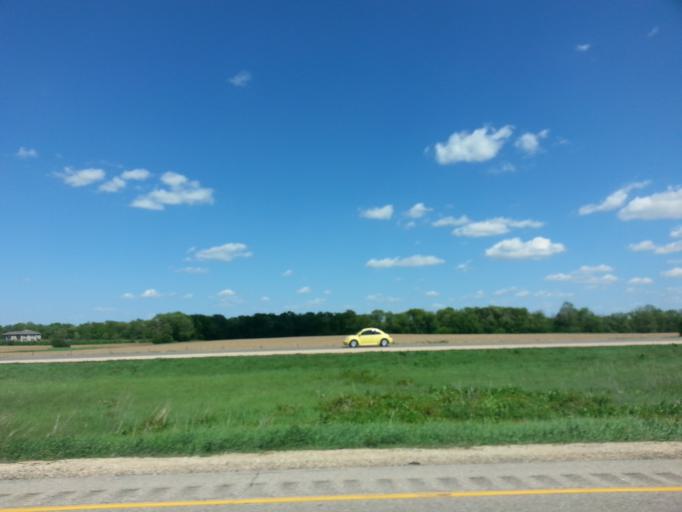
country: US
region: Wisconsin
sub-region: Rock County
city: Milton
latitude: 42.7645
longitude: -89.0050
